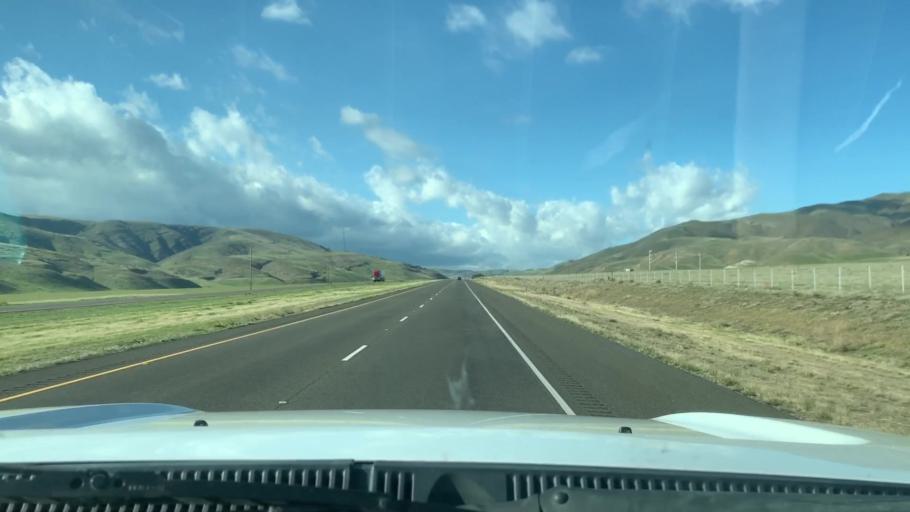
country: US
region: California
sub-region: San Luis Obispo County
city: Shandon
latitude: 35.7039
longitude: -120.1498
